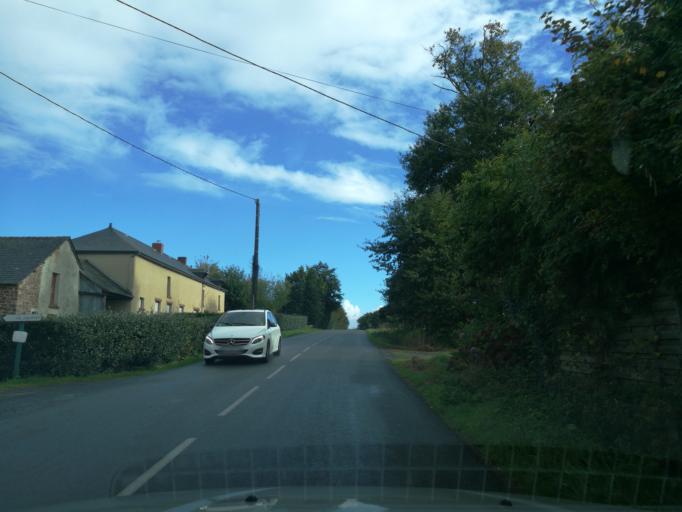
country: FR
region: Brittany
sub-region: Departement d'Ille-et-Vilaine
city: Bedee
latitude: 48.2093
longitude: -1.9385
